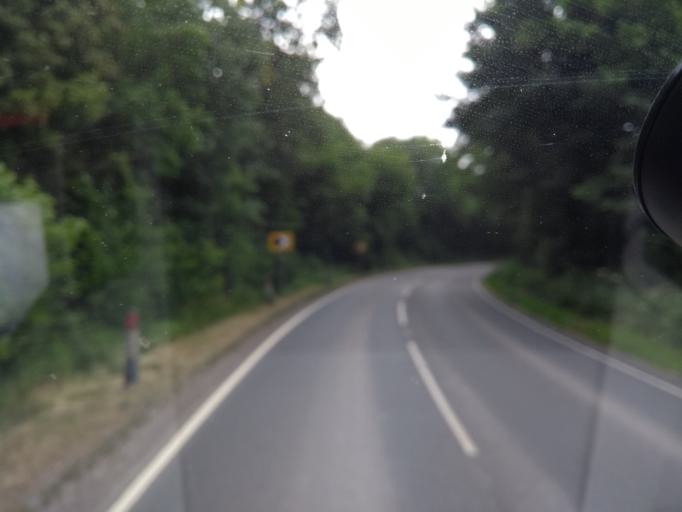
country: GB
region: England
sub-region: Somerset
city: Bridgwater
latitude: 51.1762
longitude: -3.0737
